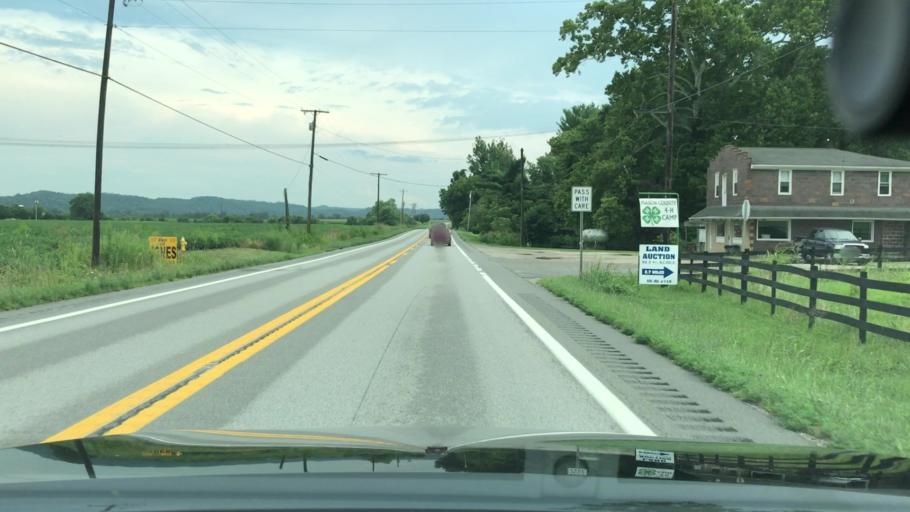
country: US
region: West Virginia
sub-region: Putnam County
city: Buffalo
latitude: 38.7450
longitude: -81.9810
